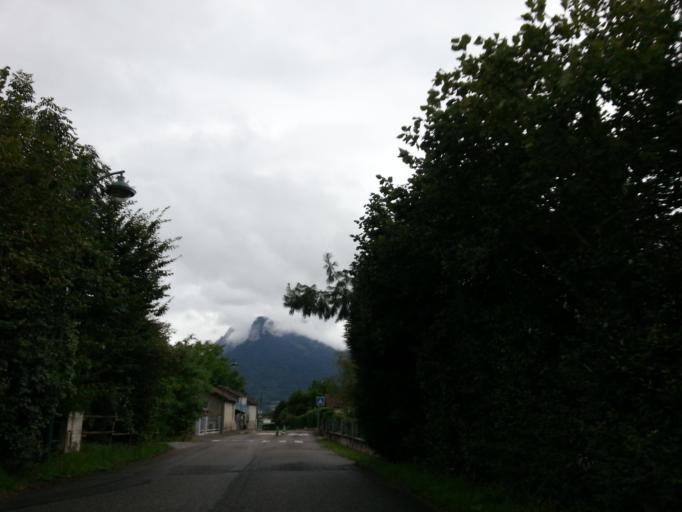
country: FR
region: Rhone-Alpes
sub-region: Departement de la Haute-Savoie
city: Doussard
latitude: 45.8060
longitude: 6.2088
